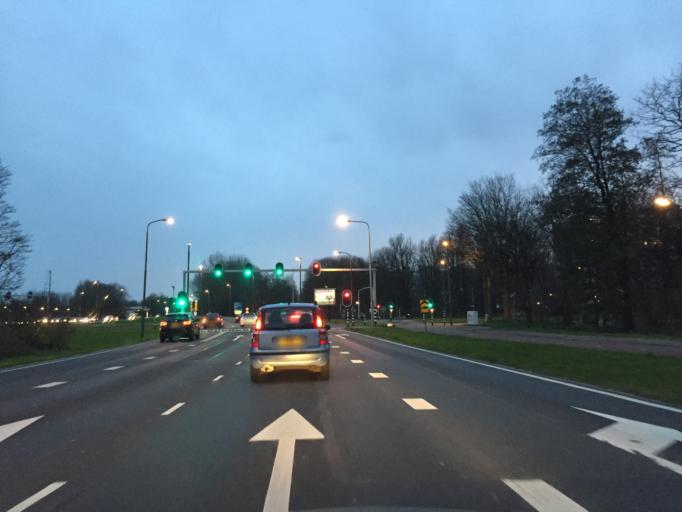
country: NL
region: South Holland
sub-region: Gemeente Delft
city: Delft
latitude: 51.9896
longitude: 4.3600
